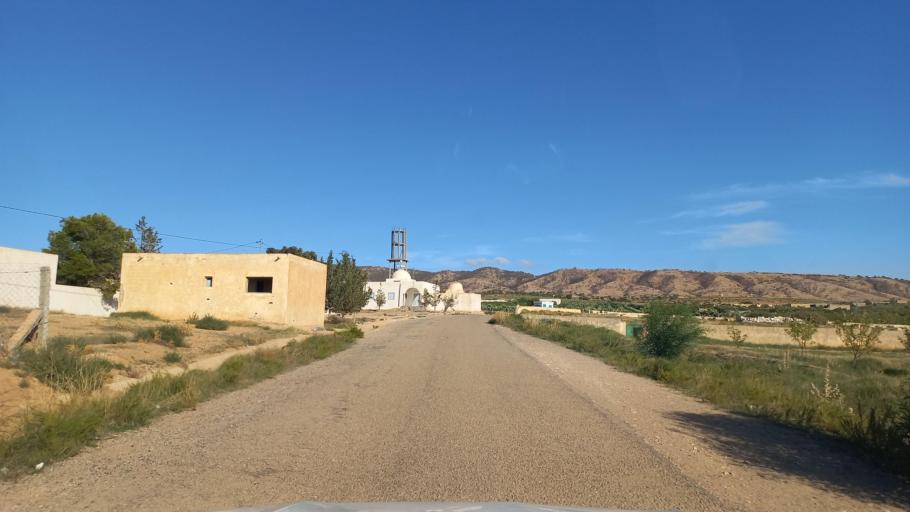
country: TN
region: Al Qasrayn
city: Sbiba
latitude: 35.3352
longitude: 9.1234
